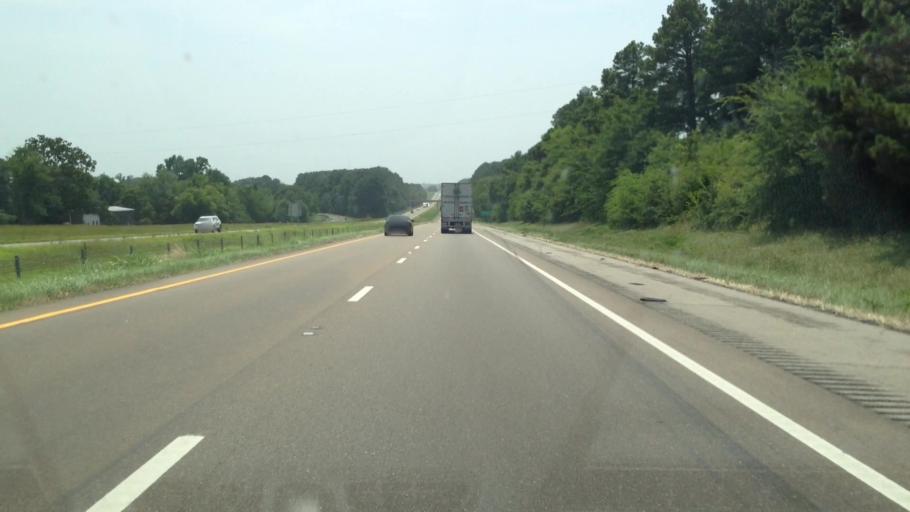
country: US
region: Texas
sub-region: Titus County
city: Mount Pleasant
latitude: 33.1917
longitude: -94.9361
